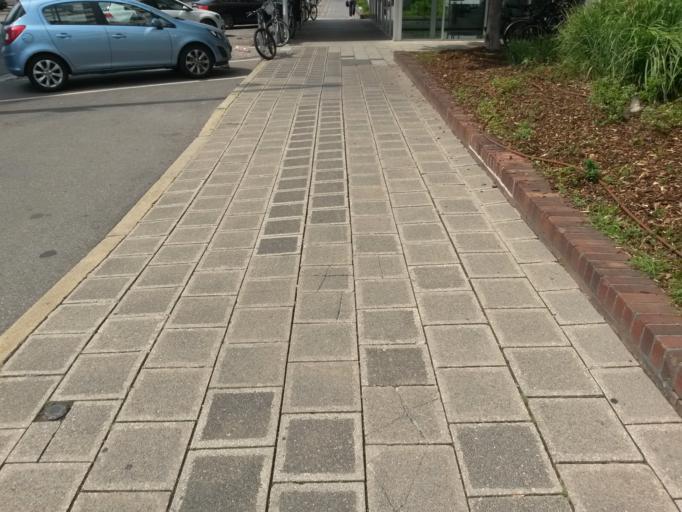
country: DE
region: Bavaria
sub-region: Regierungsbezirk Mittelfranken
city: Furth
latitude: 49.4679
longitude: 11.0131
